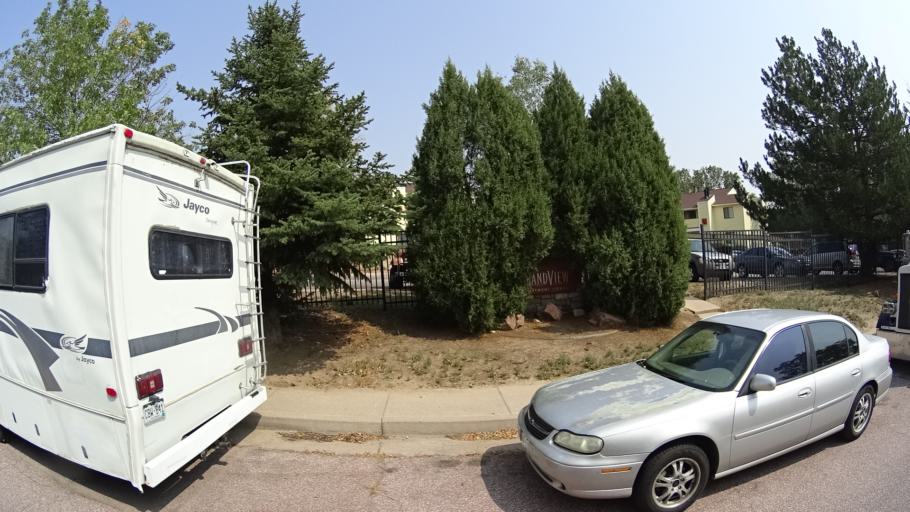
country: US
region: Colorado
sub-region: El Paso County
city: Colorado Springs
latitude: 38.8301
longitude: -104.7832
